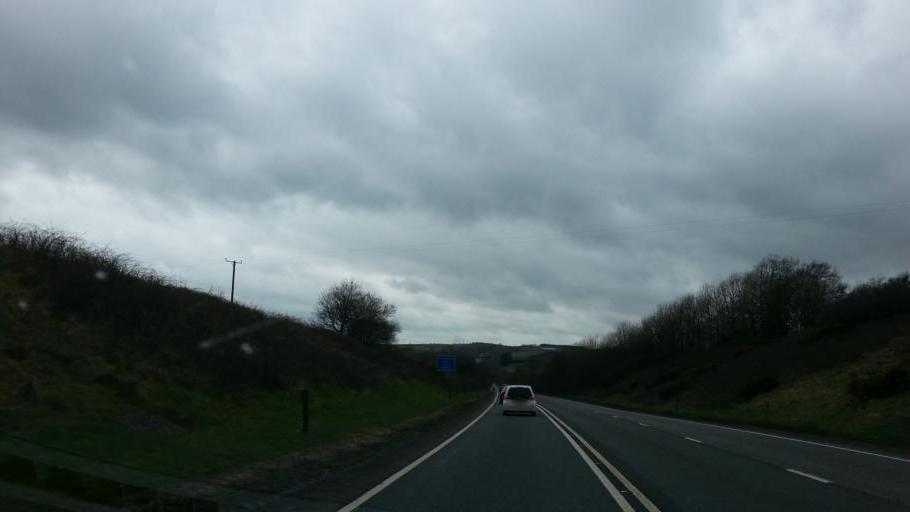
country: GB
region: England
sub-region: Devon
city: South Molton
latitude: 50.9951
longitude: -3.7151
